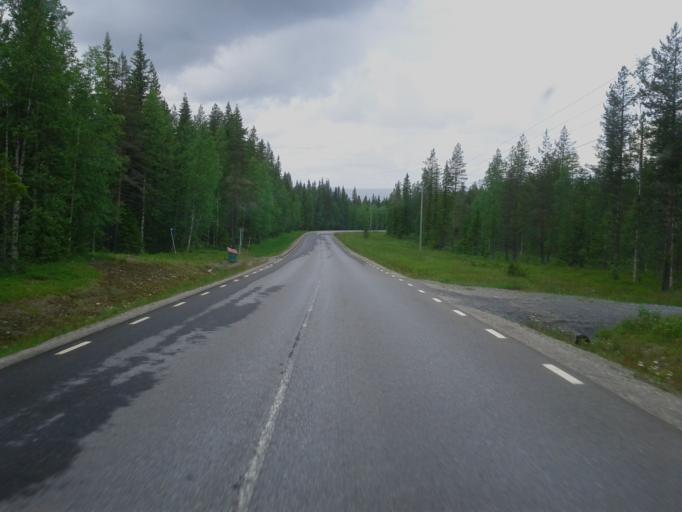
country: SE
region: Vaesterbotten
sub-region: Mala Kommun
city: Mala
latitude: 65.0735
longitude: 19.0240
